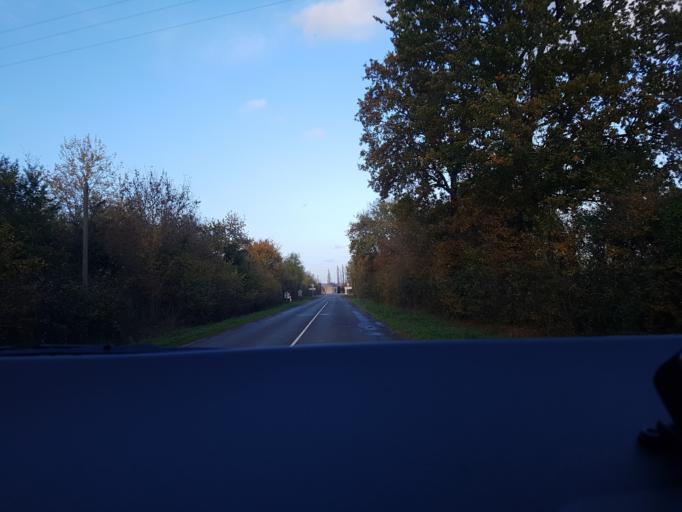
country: FR
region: Lower Normandy
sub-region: Departement du Calvados
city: Troarn
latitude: 49.2096
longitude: -0.1163
